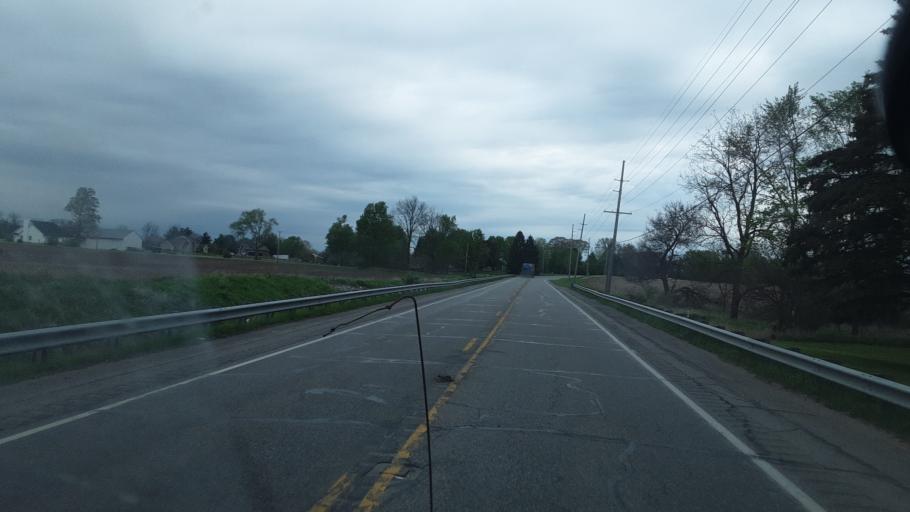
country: US
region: Indiana
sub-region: Elkhart County
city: Goshen
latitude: 41.6260
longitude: -85.8306
